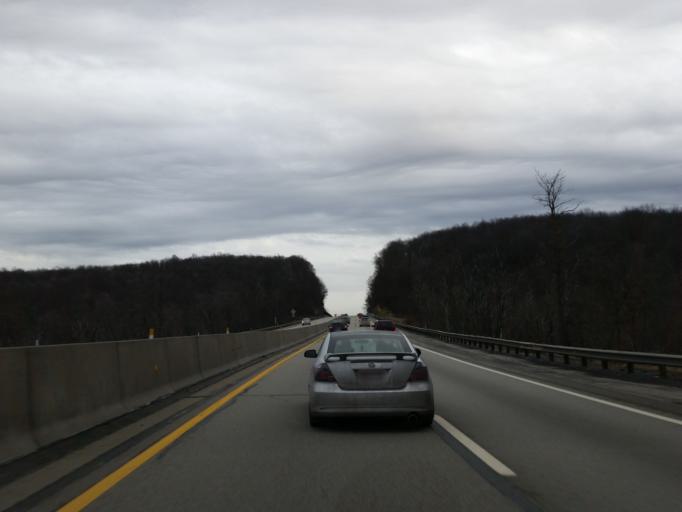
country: US
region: Pennsylvania
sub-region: Somerset County
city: Somerset
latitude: 40.0570
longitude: -79.1332
